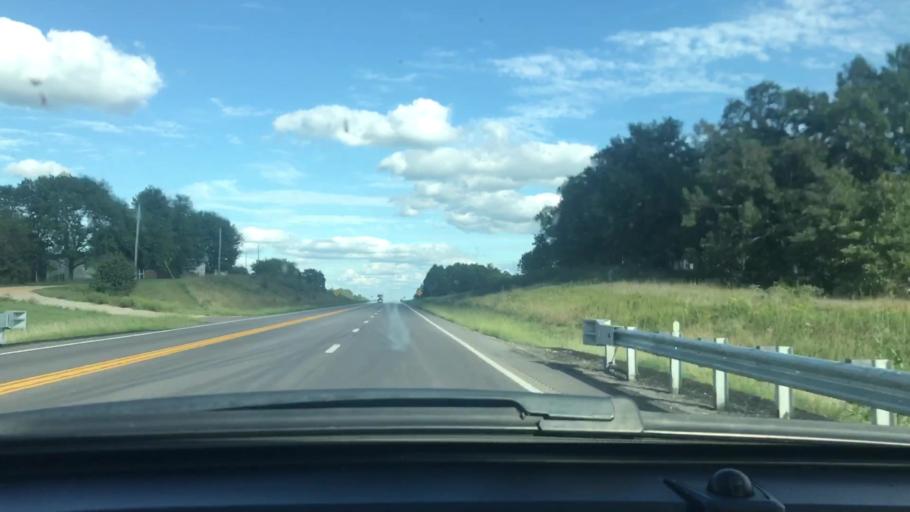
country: US
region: Missouri
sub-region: Oregon County
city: Thayer
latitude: 36.5841
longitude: -91.6155
